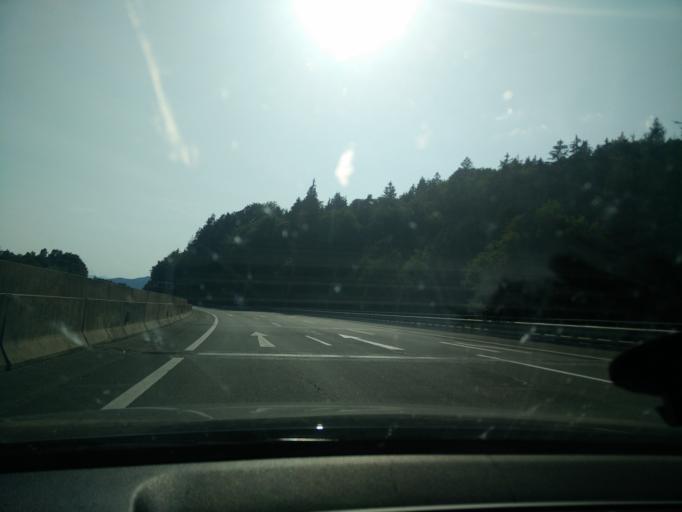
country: AT
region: Carinthia
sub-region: Politischer Bezirk Klagenfurt Land
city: Keutschach am See
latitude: 46.6309
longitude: 14.2333
